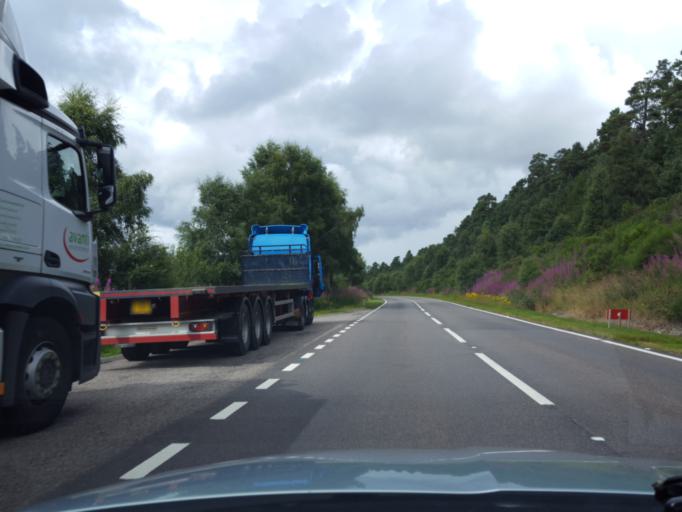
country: GB
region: Scotland
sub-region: Highland
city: Grantown on Spey
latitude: 57.2813
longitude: -3.6777
